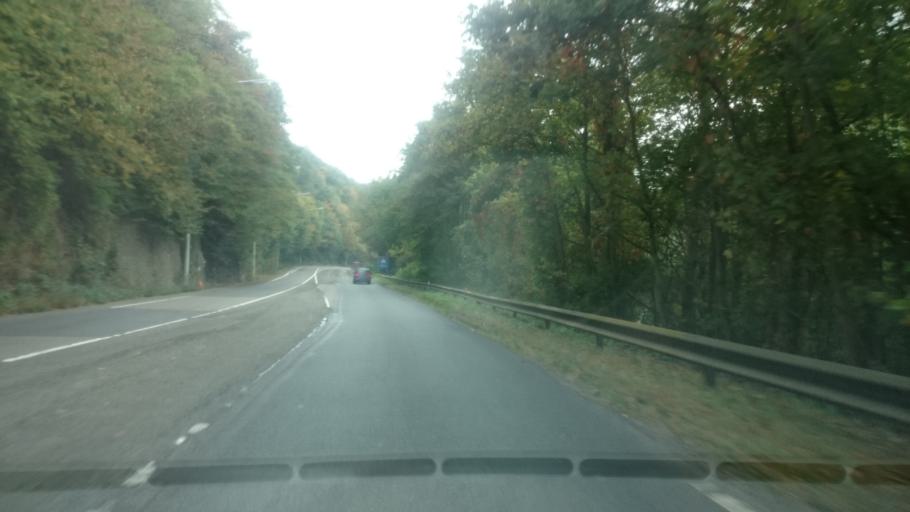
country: BE
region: Wallonia
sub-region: Province de Namur
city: Namur
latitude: 50.4567
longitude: 4.8351
